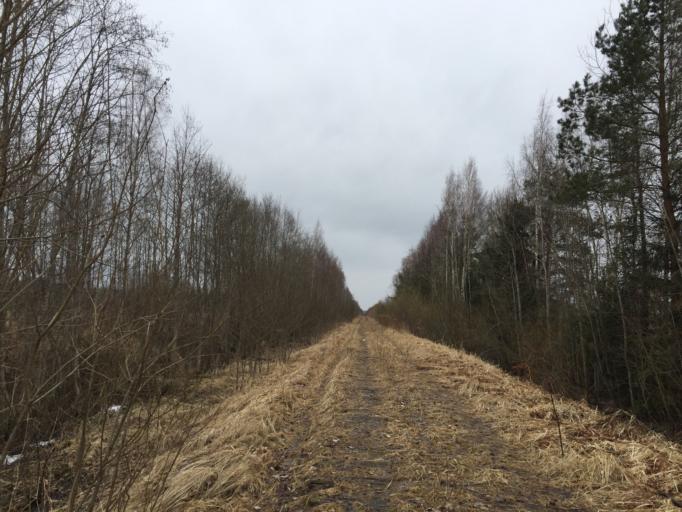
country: LV
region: Lielvarde
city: Lielvarde
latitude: 56.7597
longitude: 24.8180
